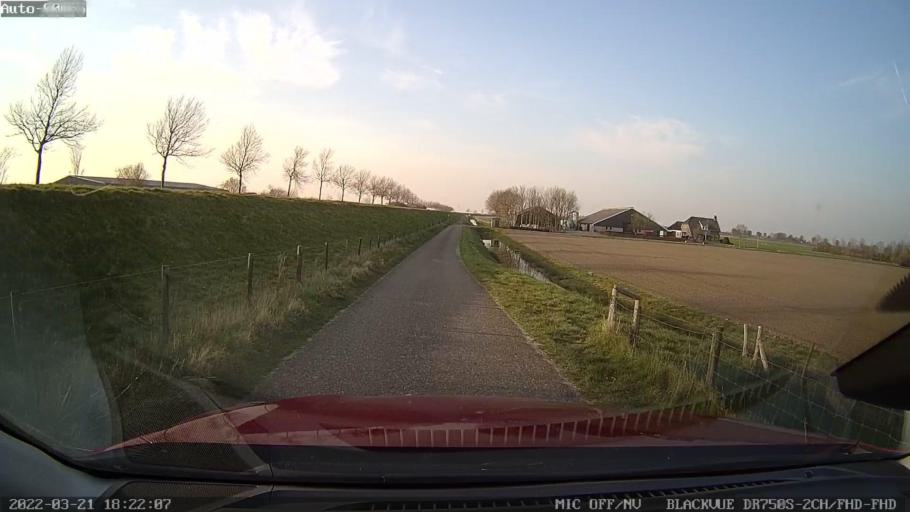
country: NL
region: North Brabant
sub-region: Gemeente Steenbergen
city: Nieuw-Vossemeer
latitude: 51.5892
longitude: 4.2036
